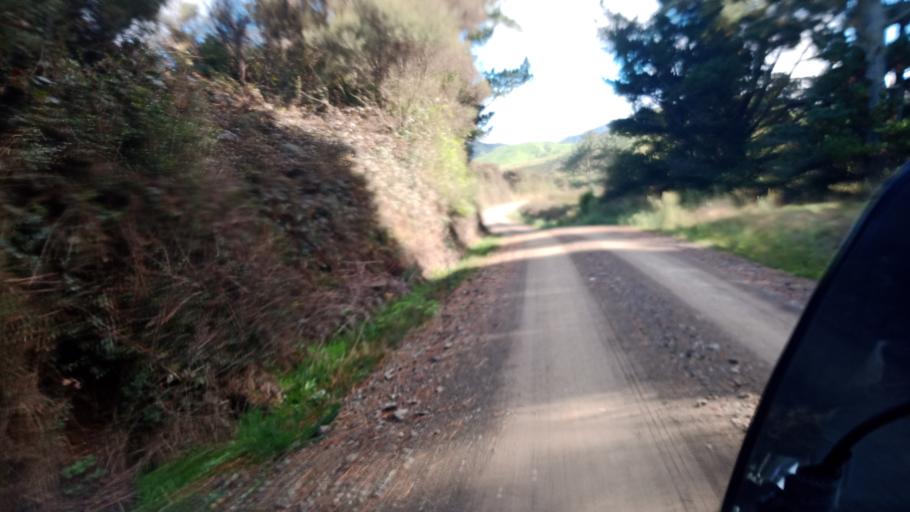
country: NZ
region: Bay of Plenty
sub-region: Opotiki District
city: Opotiki
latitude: -38.4604
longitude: 177.4189
